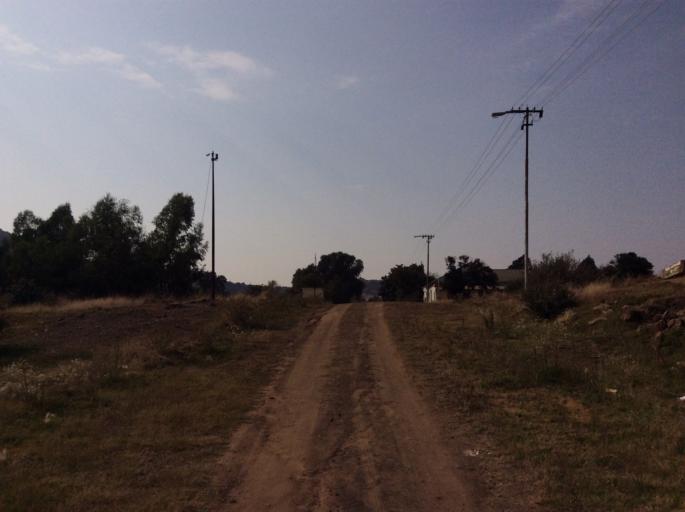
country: LS
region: Mafeteng
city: Mafeteng
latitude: -29.7252
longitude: 27.0350
